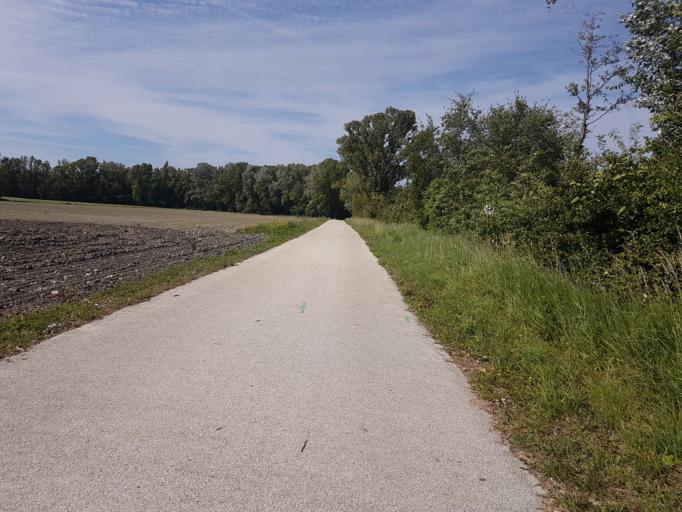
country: FR
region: Rhone-Alpes
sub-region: Departement de l'Ardeche
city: La Voulte-sur-Rhone
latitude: 44.7785
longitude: 4.7697
